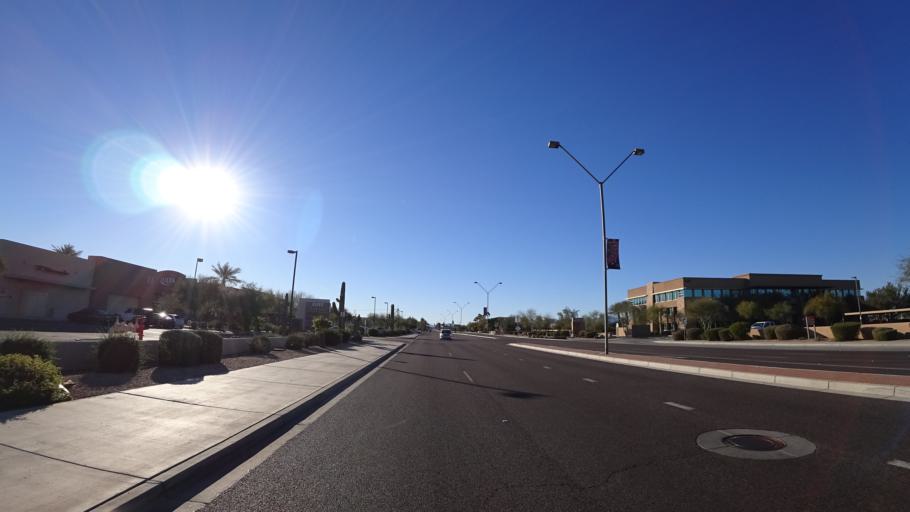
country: US
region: Arizona
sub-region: Maricopa County
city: Goodyear
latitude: 33.4643
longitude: -112.3603
